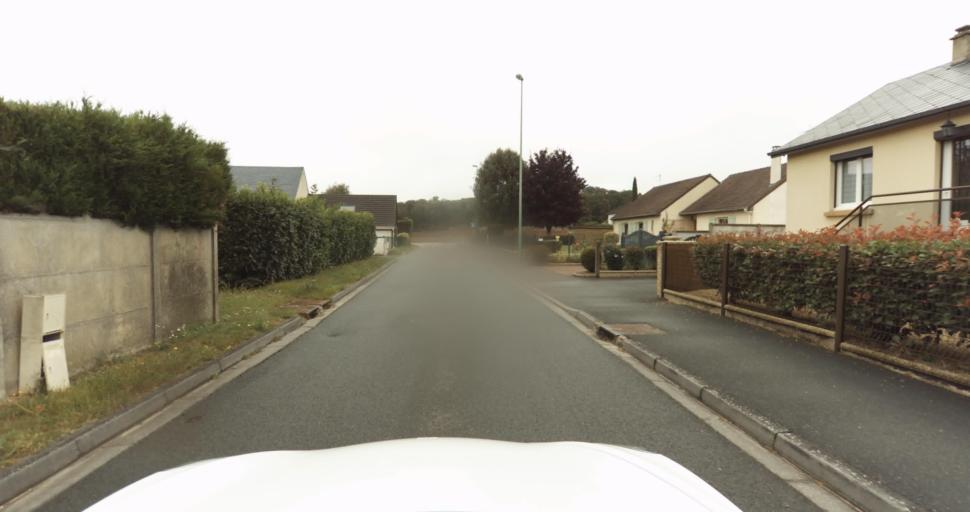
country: FR
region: Haute-Normandie
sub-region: Departement de l'Eure
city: Aviron
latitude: 49.0518
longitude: 1.1252
